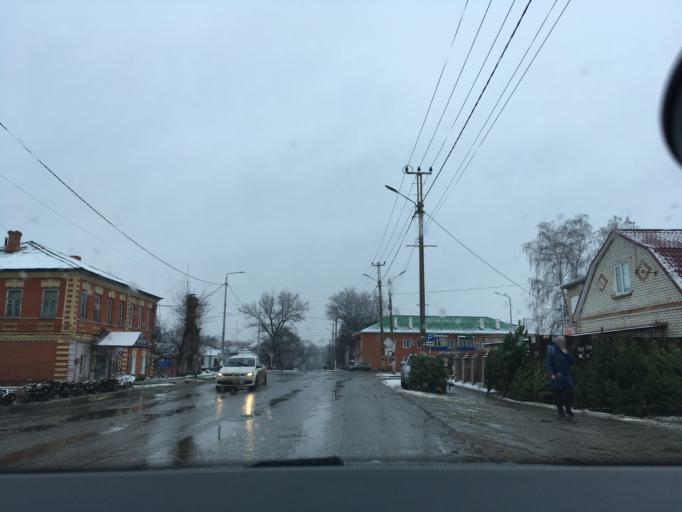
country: RU
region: Belgorod
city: Valuyki
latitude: 50.2067
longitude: 38.1059
